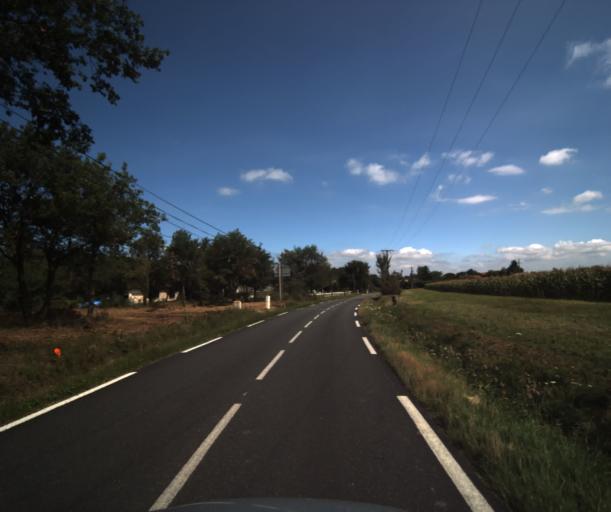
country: FR
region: Midi-Pyrenees
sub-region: Departement de la Haute-Garonne
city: Lacasse
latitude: 43.3880
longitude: 1.2495
